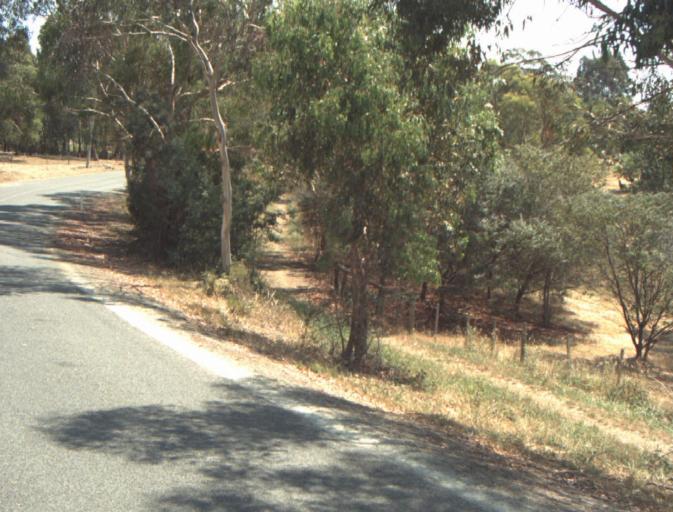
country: AU
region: Tasmania
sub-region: Launceston
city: Newstead
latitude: -41.4894
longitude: 147.1988
